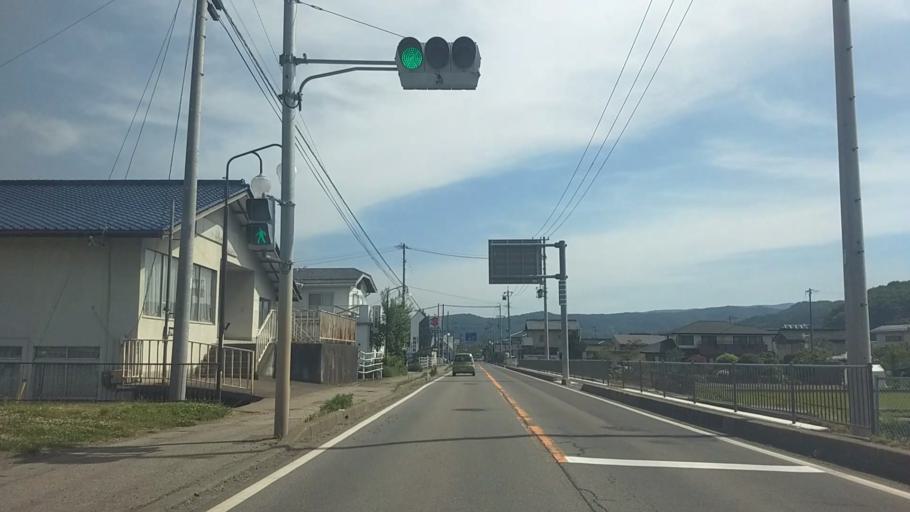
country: JP
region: Nagano
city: Saku
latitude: 36.1619
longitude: 138.4828
